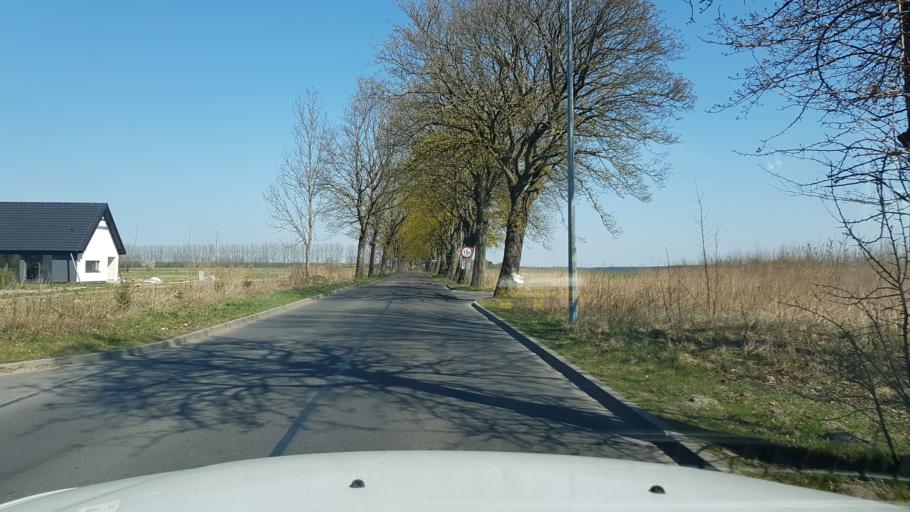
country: PL
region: West Pomeranian Voivodeship
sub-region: Powiat slawienski
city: Slawno
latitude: 54.3739
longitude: 16.6820
